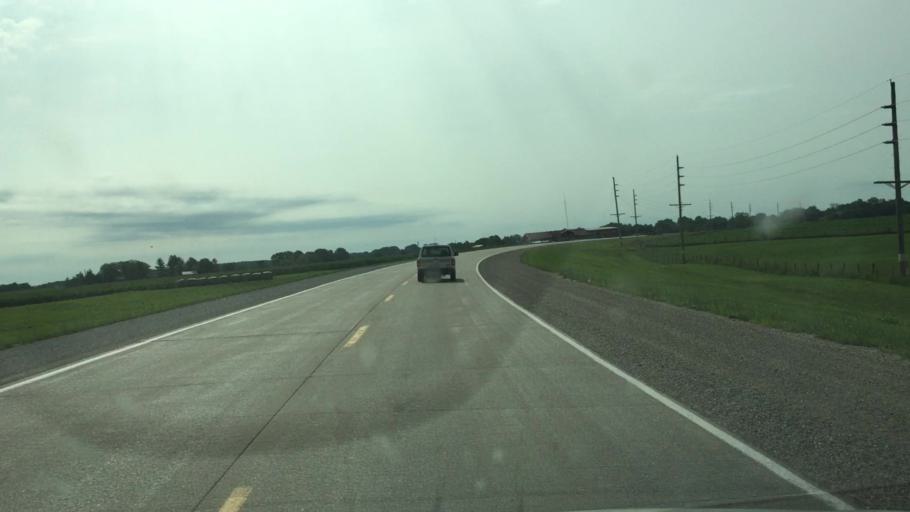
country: US
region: Illinois
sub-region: Hancock County
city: Nauvoo
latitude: 40.6387
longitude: -91.5233
